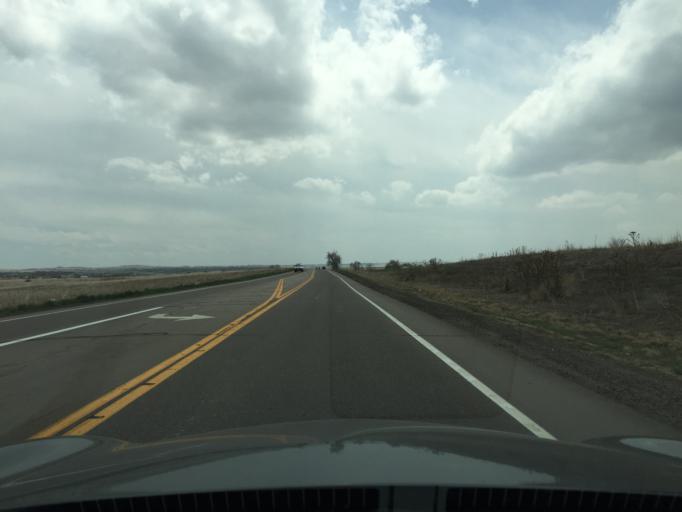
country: US
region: Colorado
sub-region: Boulder County
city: Erie
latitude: 40.0287
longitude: -105.0553
